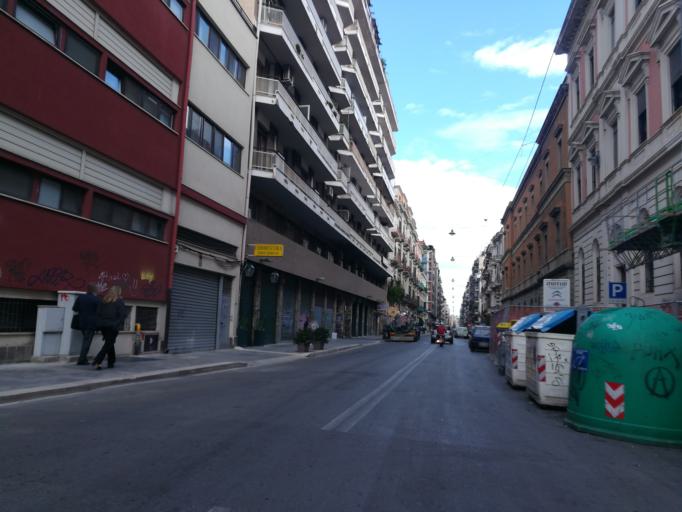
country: IT
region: Apulia
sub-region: Provincia di Bari
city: Bari
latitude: 41.1184
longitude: 16.8718
